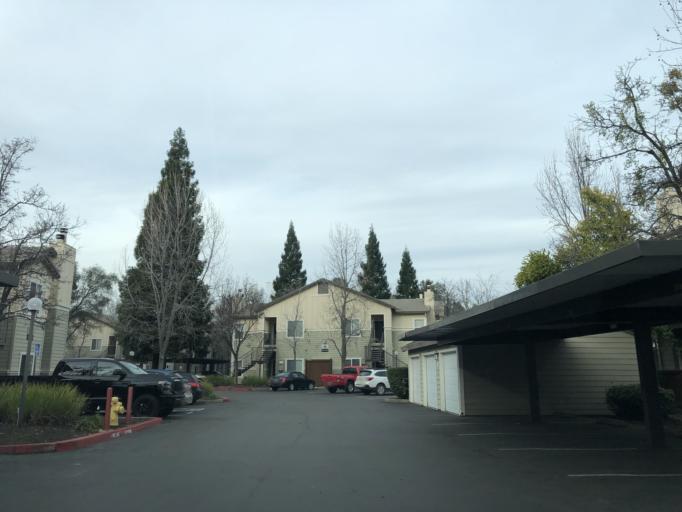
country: US
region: California
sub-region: Sacramento County
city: Folsom
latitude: 38.6496
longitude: -121.1813
